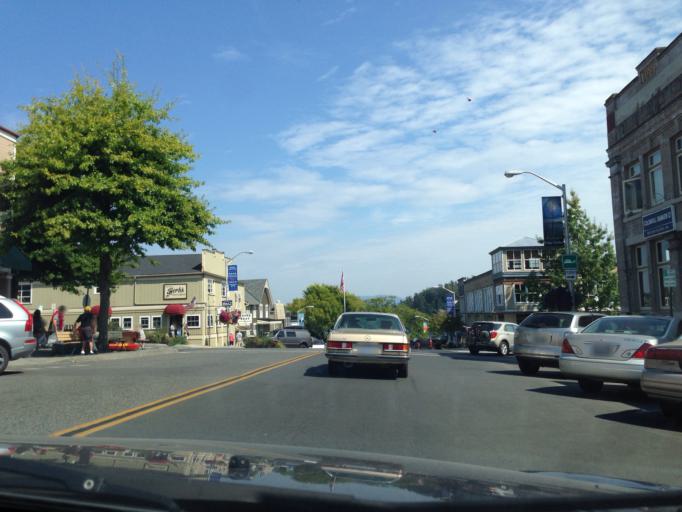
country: US
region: Washington
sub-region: San Juan County
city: Friday Harbor
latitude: 48.5345
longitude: -123.0164
